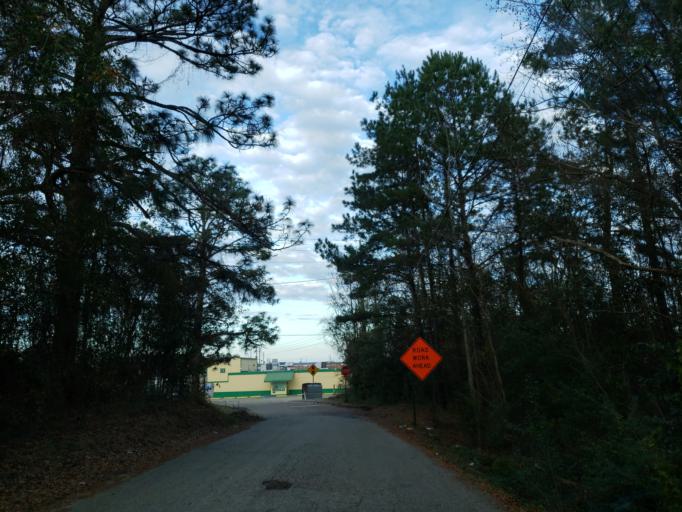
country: US
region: Mississippi
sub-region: Forrest County
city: Hattiesburg
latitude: 31.3037
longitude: -89.3147
